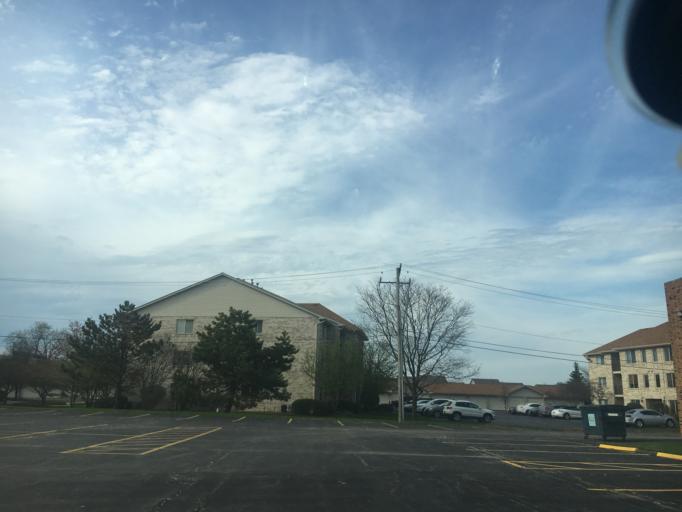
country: US
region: Illinois
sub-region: Cook County
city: Tinley Park
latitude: 41.6130
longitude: -87.7873
